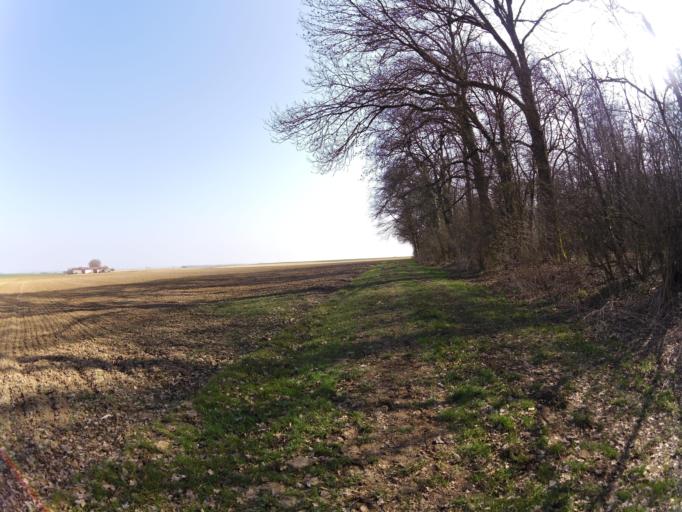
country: DE
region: Bavaria
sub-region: Regierungsbezirk Unterfranken
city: Geroldshausen
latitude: 49.6746
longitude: 9.9115
